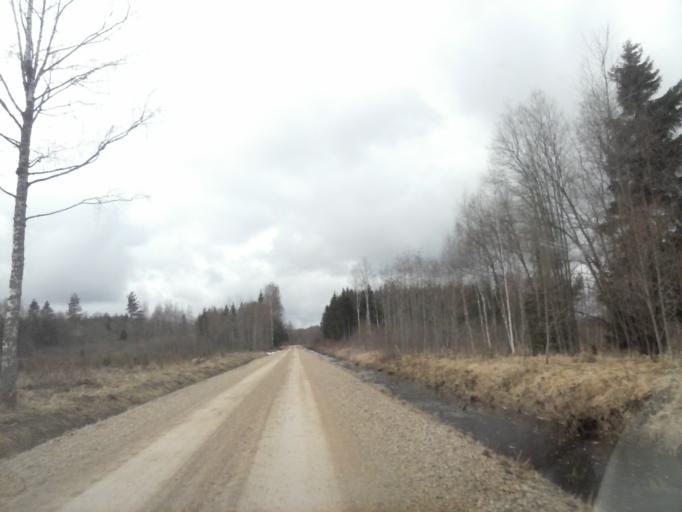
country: EE
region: Jogevamaa
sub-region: Mustvee linn
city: Mustvee
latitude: 59.0949
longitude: 26.8272
